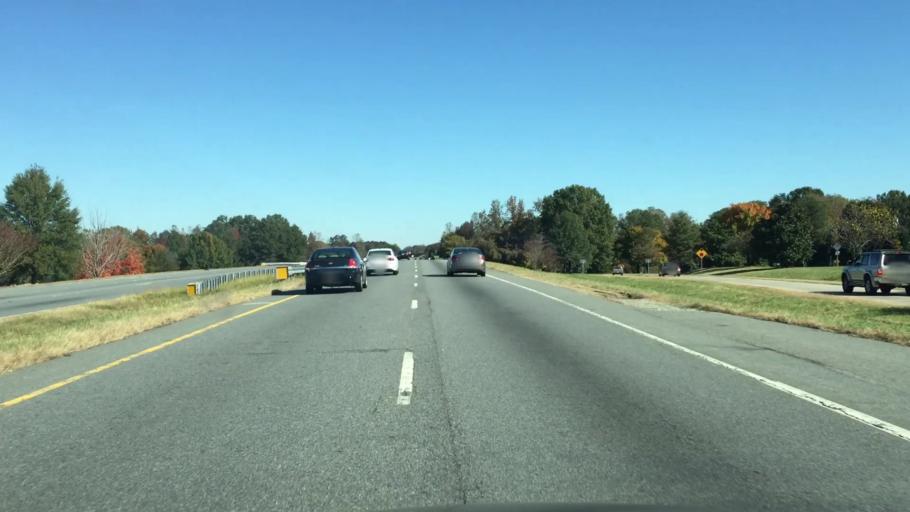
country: US
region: North Carolina
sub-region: Guilford County
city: McLeansville
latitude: 36.2123
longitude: -79.6889
